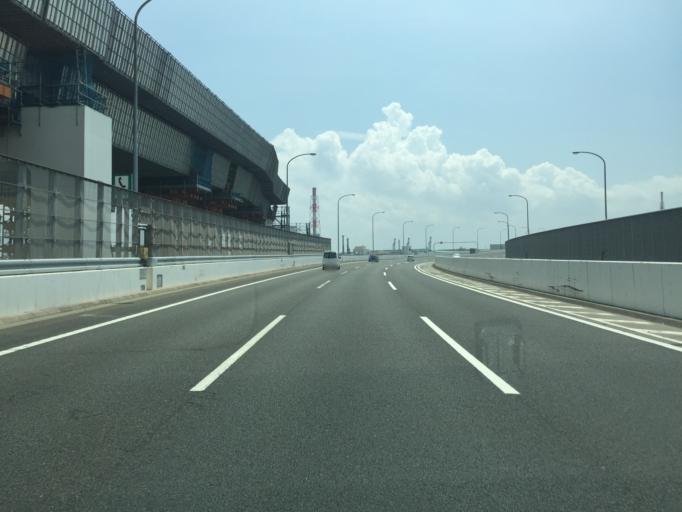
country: JP
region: Kanagawa
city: Yokohama
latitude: 35.4188
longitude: 139.6706
